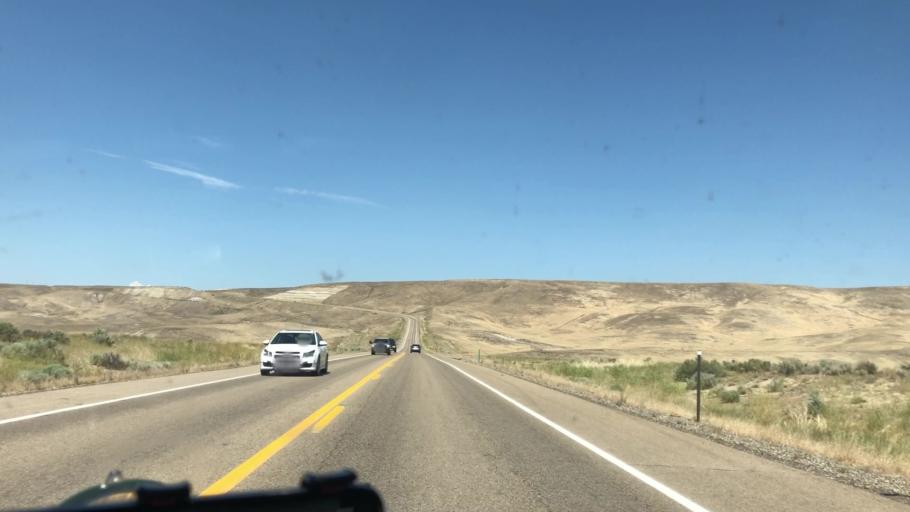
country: US
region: Idaho
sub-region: Owyhee County
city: Marsing
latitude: 43.2782
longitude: -116.9955
